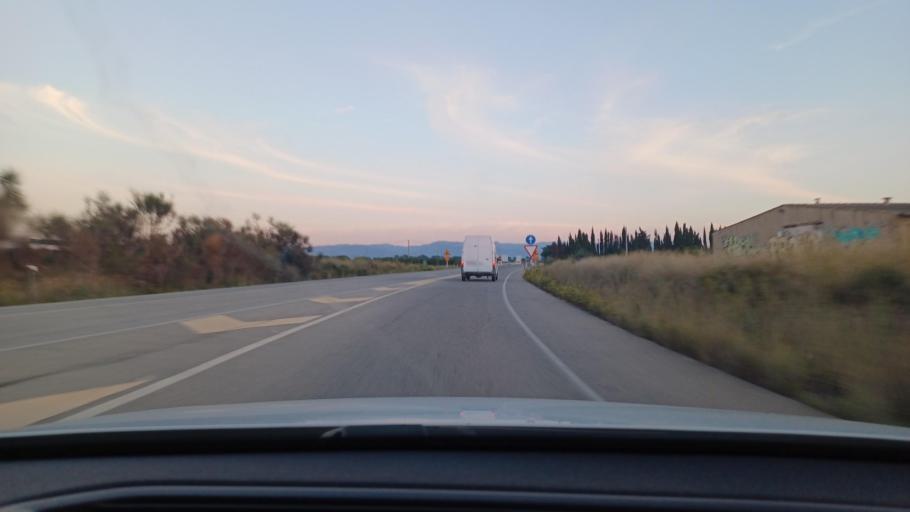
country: ES
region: Catalonia
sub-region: Provincia de Tarragona
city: Alcanar
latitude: 40.5466
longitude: 0.4358
